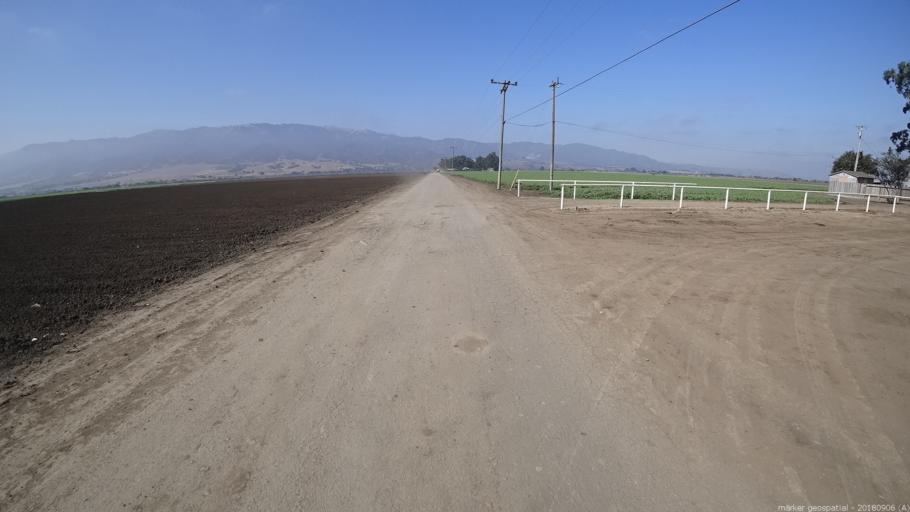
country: US
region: California
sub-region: Monterey County
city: Chualar
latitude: 36.5886
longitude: -121.5604
